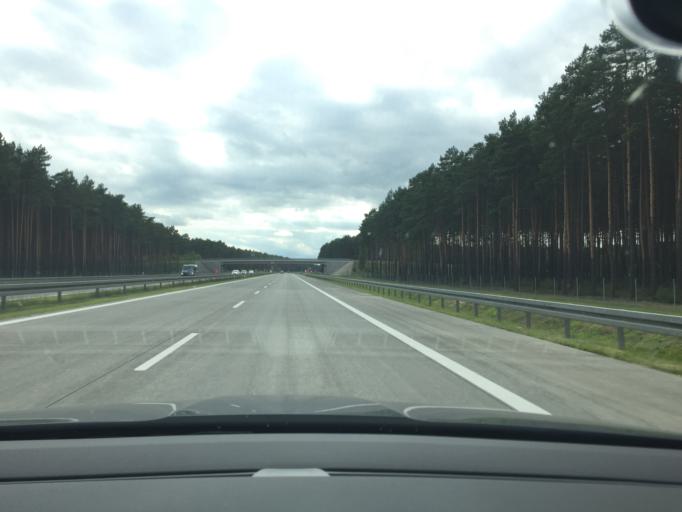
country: PL
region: Greater Poland Voivodeship
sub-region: Powiat nowotomyski
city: Miedzichowo
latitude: 52.3374
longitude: 15.9751
